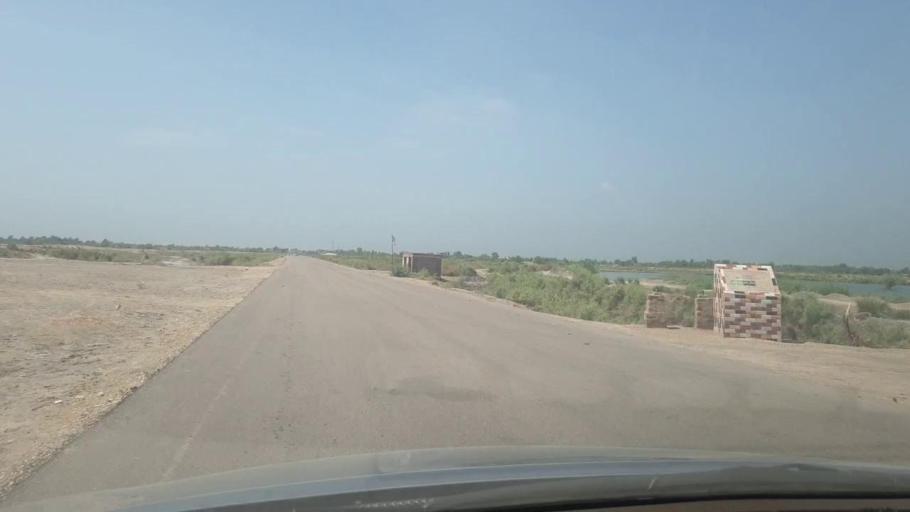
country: PK
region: Sindh
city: Ranipur
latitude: 27.2374
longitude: 68.5715
